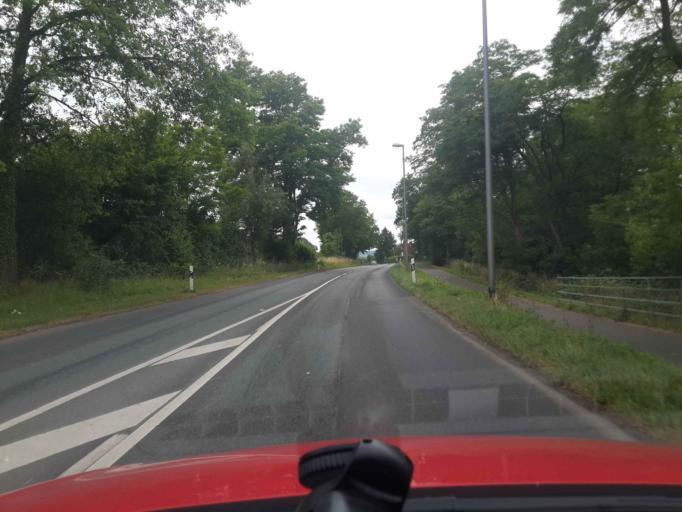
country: DE
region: Bavaria
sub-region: Regierungsbezirk Unterfranken
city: Aschaffenburg
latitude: 49.9574
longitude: 9.1315
